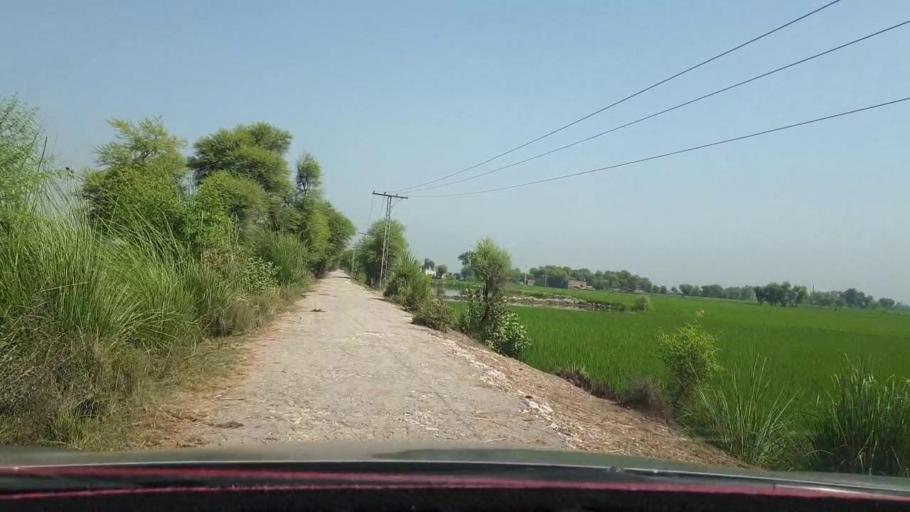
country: PK
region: Sindh
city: Warah
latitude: 27.4946
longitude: 67.8356
